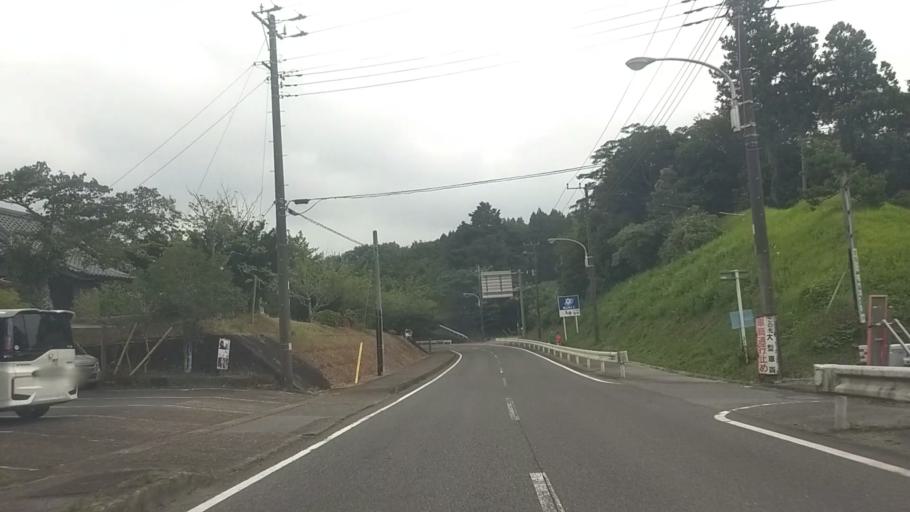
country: JP
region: Chiba
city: Kawaguchi
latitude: 35.2290
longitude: 140.0894
